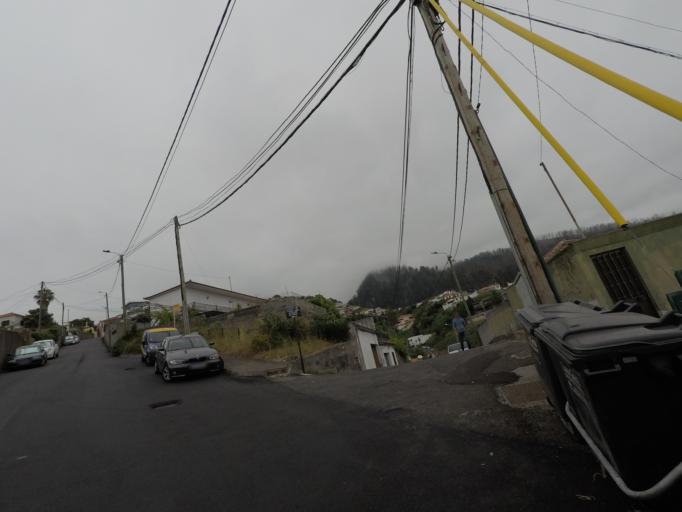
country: PT
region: Madeira
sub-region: Funchal
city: Nossa Senhora do Monte
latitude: 32.6728
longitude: -16.9384
